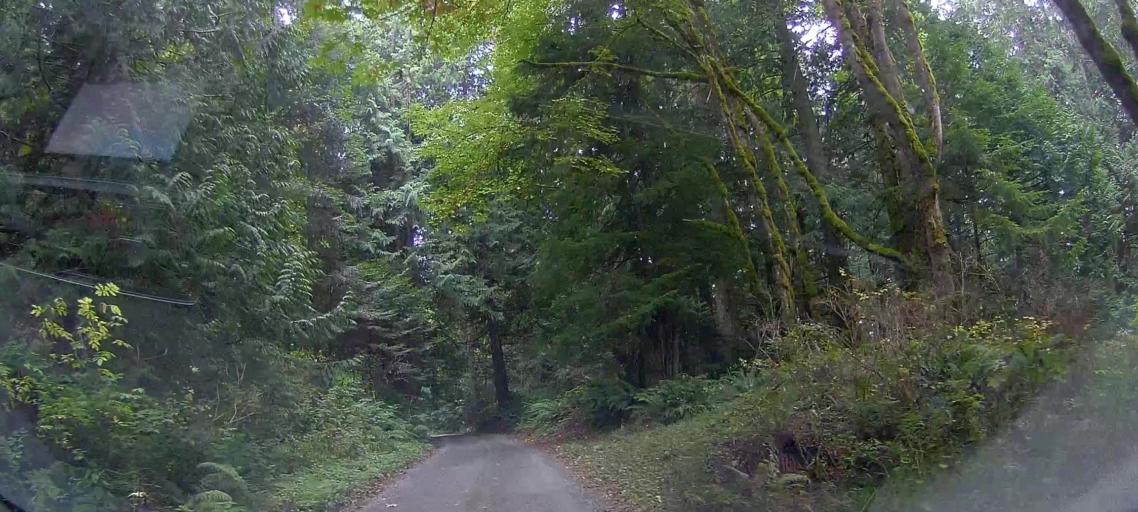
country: US
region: Washington
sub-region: Whatcom County
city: Geneva
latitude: 48.6199
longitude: -122.4371
